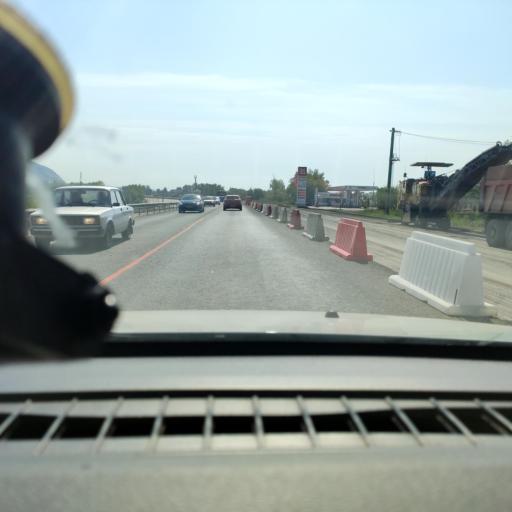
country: RU
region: Samara
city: Volzhskiy
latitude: 53.4213
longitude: 50.1266
